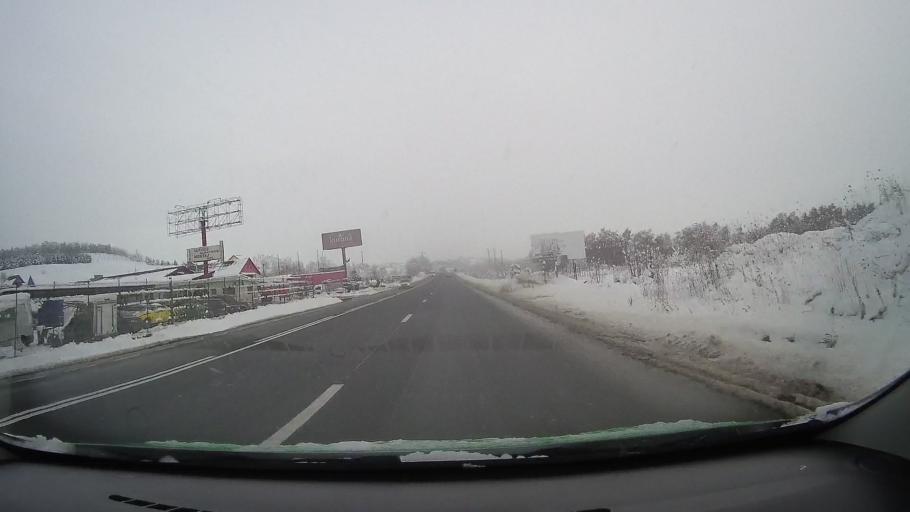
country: RO
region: Sibiu
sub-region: Comuna Cristian
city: Cristian
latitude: 45.7883
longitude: 24.0436
